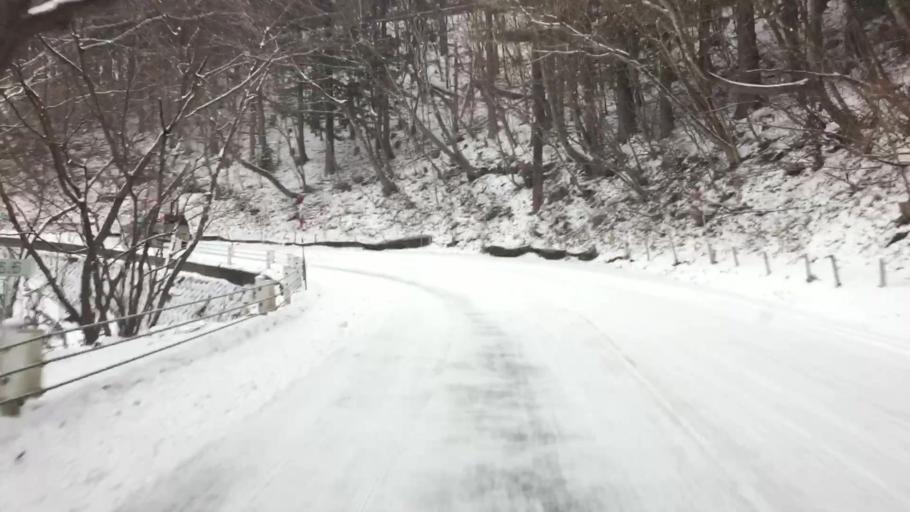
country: JP
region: Tochigi
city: Imaichi
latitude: 36.8821
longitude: 139.7326
